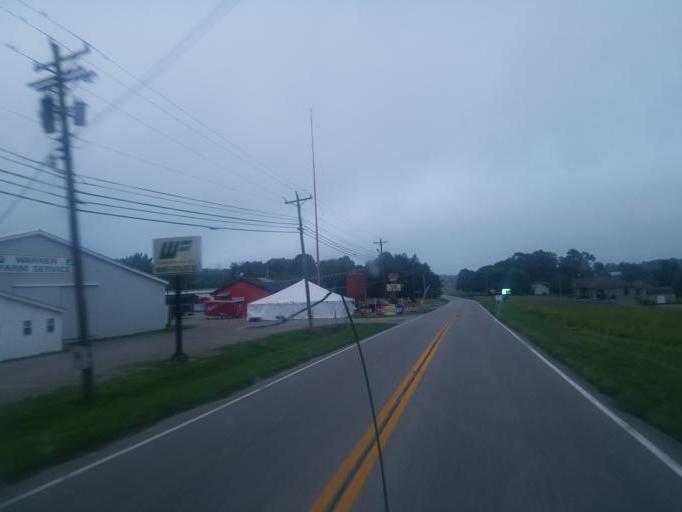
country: US
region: Kentucky
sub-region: Clinton County
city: Albany
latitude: 36.7266
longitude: -85.1338
